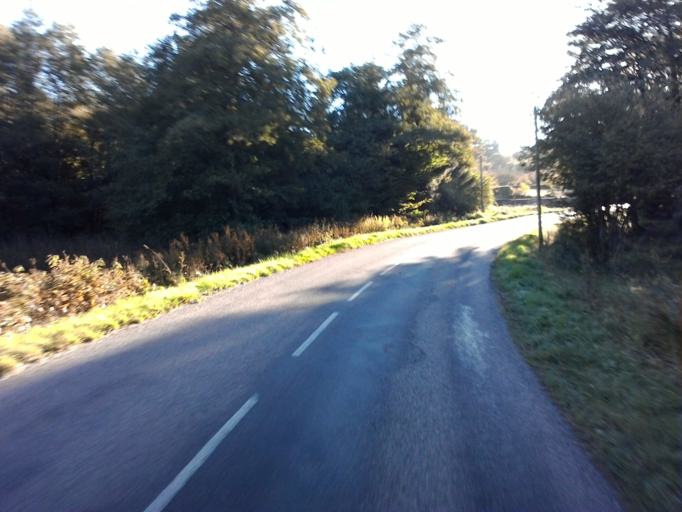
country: FR
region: Bourgogne
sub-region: Departement de la Cote-d'Or
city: Saulieu
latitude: 47.2794
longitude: 4.0915
